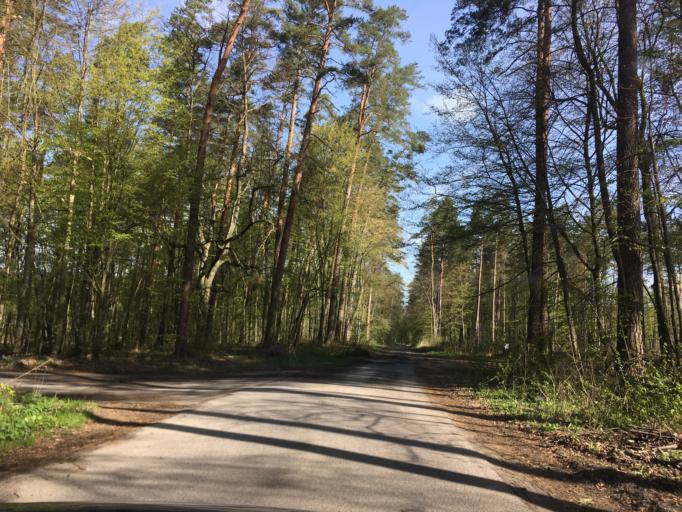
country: PL
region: Warmian-Masurian Voivodeship
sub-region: Powiat piski
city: Ruciane-Nida
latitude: 53.6870
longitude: 21.5890
